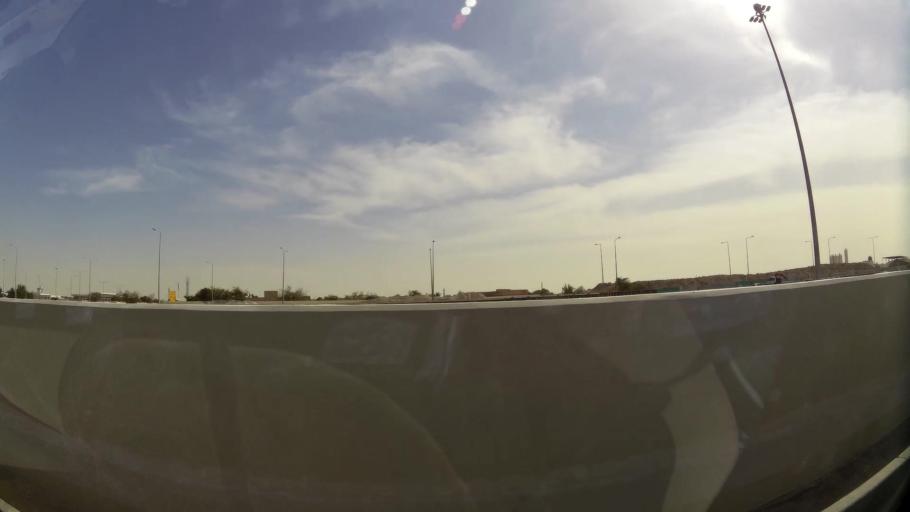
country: QA
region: Baladiyat ar Rayyan
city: Ar Rayyan
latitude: 25.3010
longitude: 51.4278
